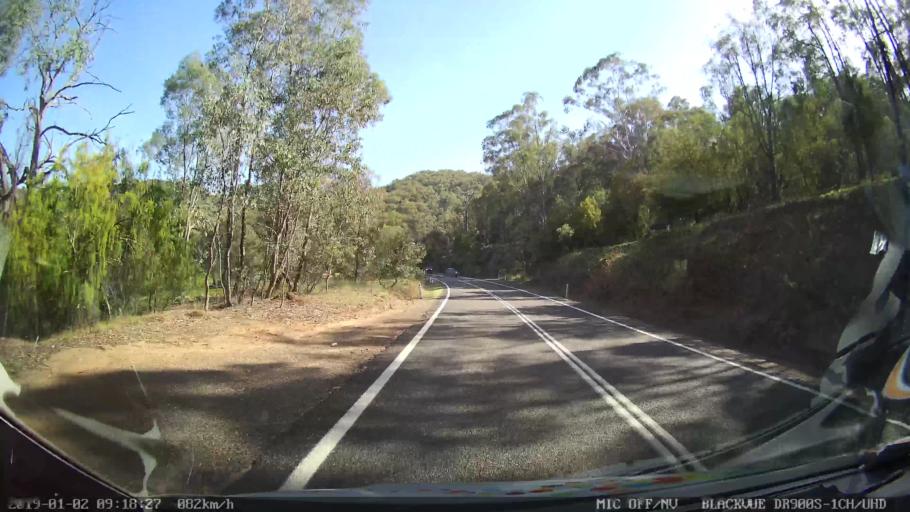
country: AU
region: New South Wales
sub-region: Tumut Shire
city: Tumut
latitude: -35.4289
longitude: 148.2866
